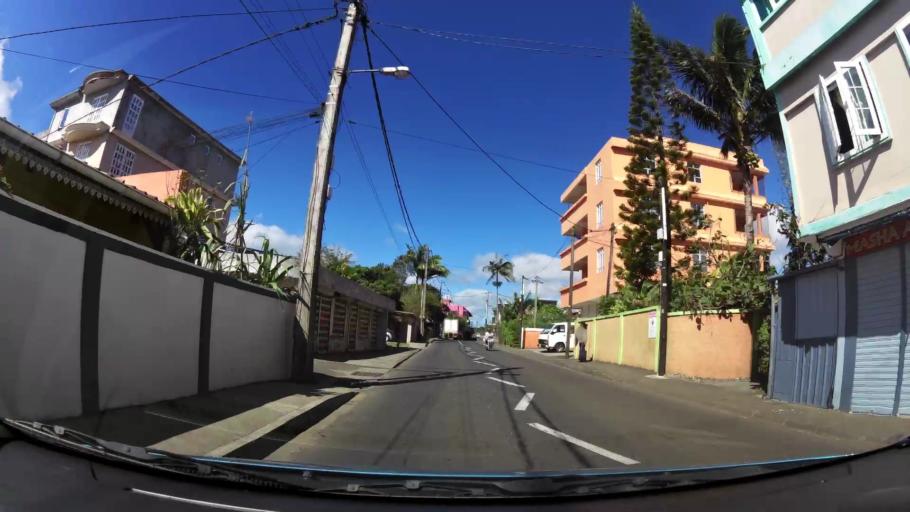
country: MU
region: Plaines Wilhems
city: Vacoas
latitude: -20.3259
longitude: 57.4857
